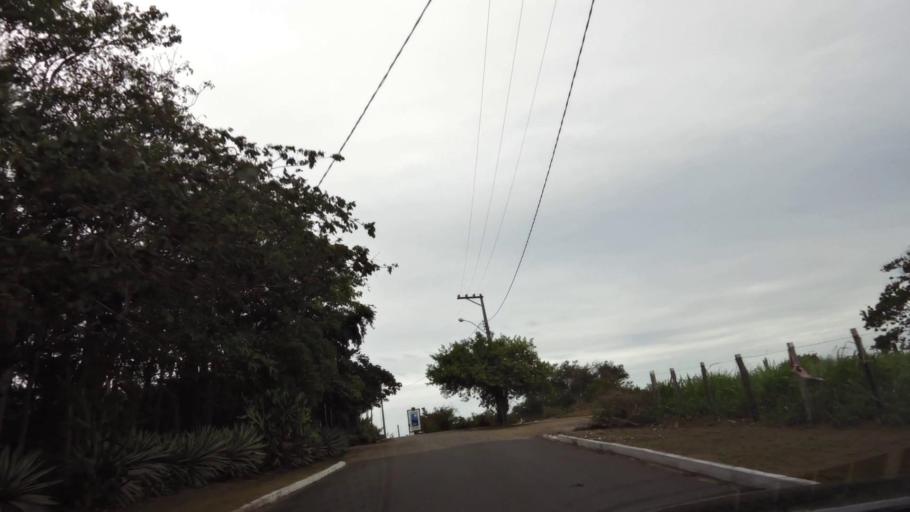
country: BR
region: Espirito Santo
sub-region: Piuma
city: Piuma
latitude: -20.8024
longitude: -40.5865
